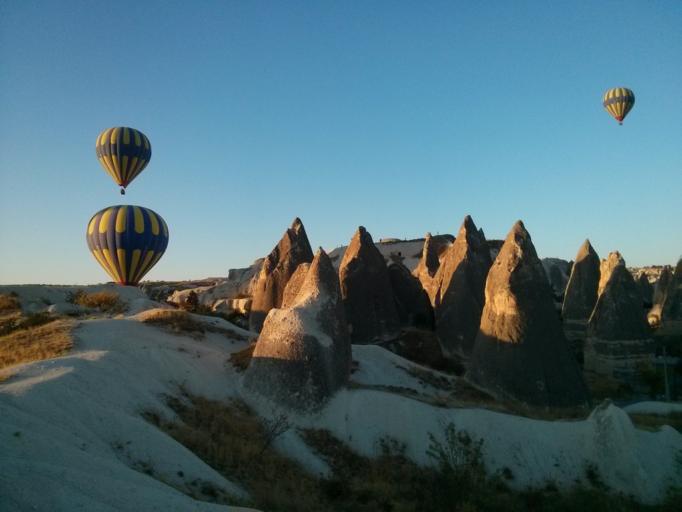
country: TR
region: Nevsehir
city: Goereme
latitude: 38.6456
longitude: 34.8358
